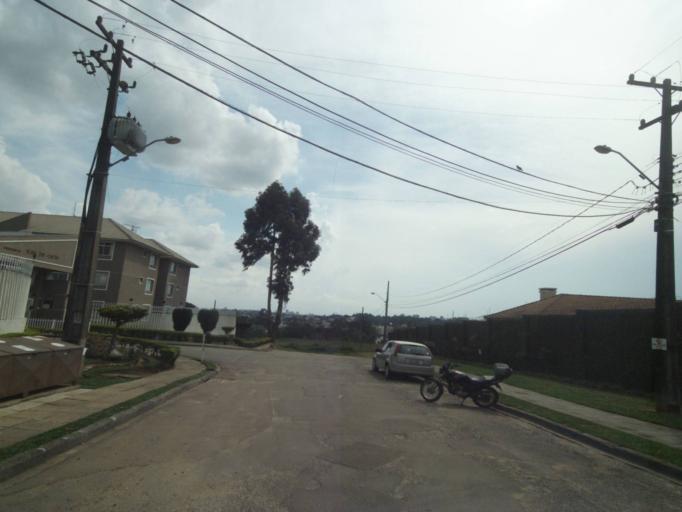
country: BR
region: Parana
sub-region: Pinhais
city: Pinhais
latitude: -25.4056
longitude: -49.2126
